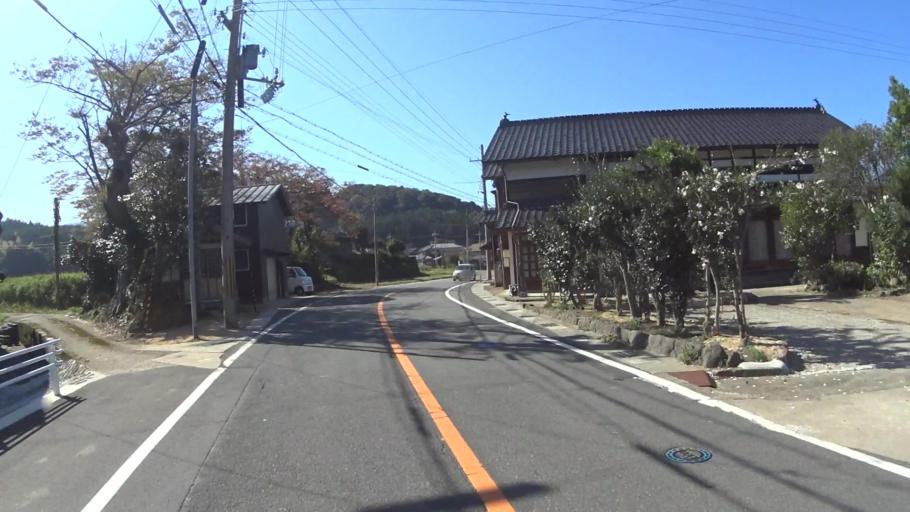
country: JP
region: Kyoto
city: Miyazu
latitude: 35.7519
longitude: 135.1700
